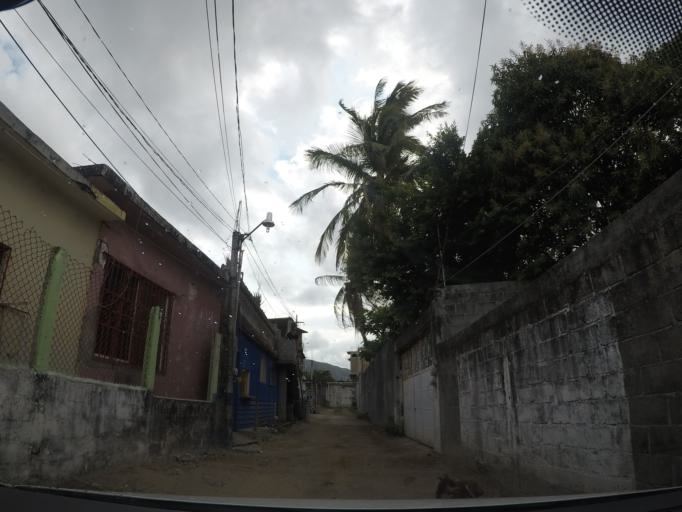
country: MX
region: Oaxaca
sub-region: Salina Cruz
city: Salina Cruz
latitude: 16.2102
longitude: -95.2076
